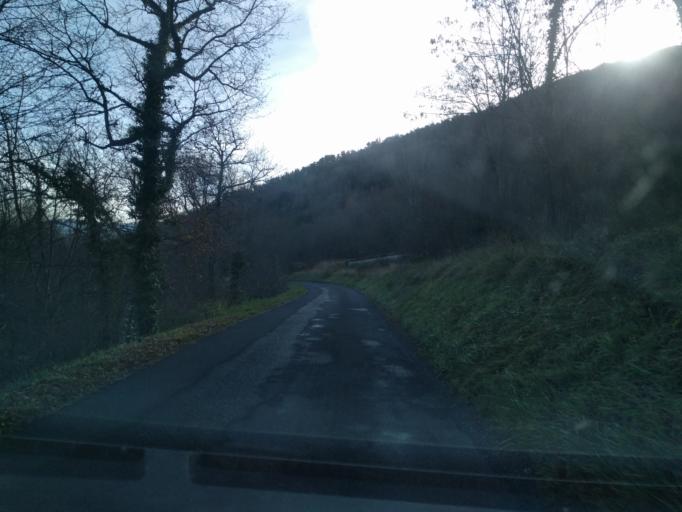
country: FR
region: Languedoc-Roussillon
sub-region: Departement de l'Aude
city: Quillan
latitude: 42.8979
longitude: 2.1859
